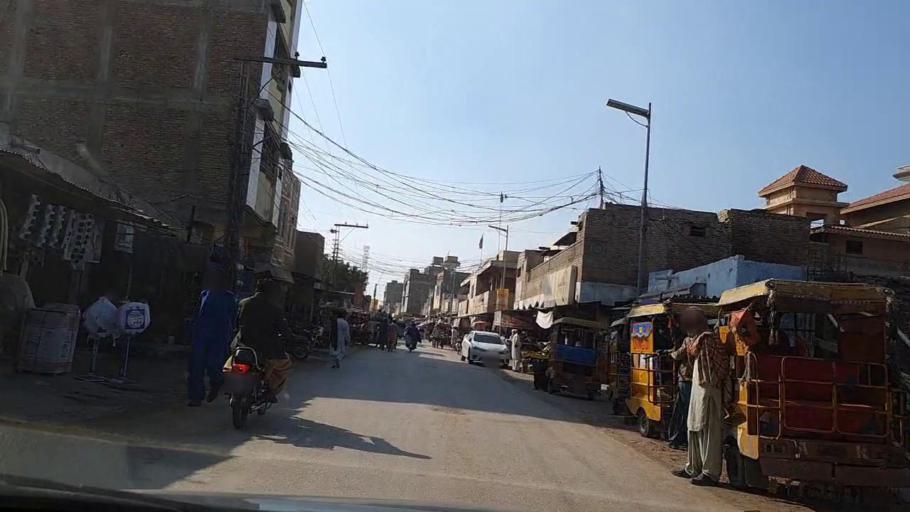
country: PK
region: Sindh
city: Sakrand
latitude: 26.1360
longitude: 68.2726
